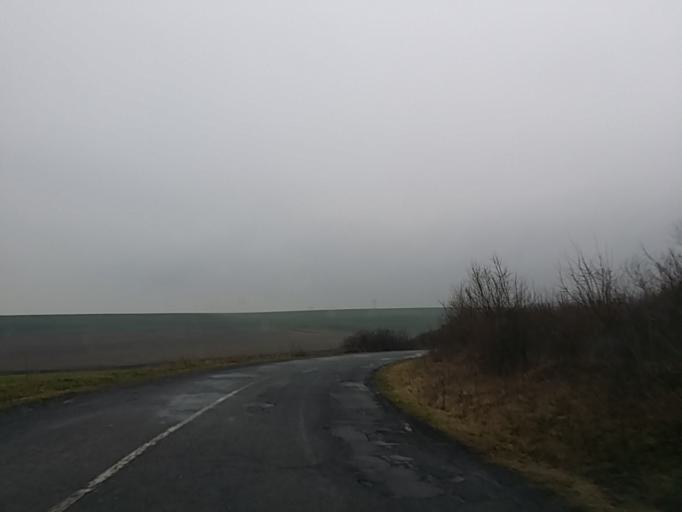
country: HU
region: Borsod-Abauj-Zemplen
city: Saly
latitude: 47.9043
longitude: 20.6501
